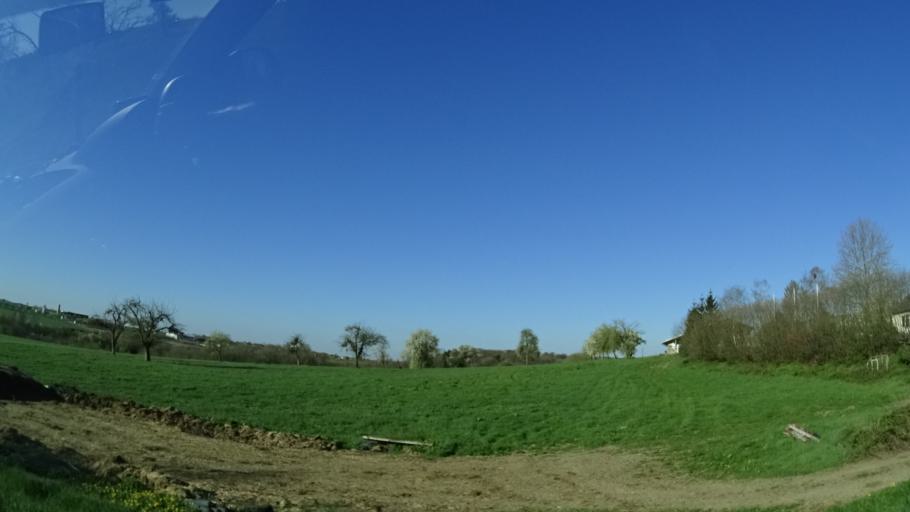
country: DE
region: Baden-Wuerttemberg
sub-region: Regierungsbezirk Stuttgart
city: Wolpertshausen
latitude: 49.1785
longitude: 9.8573
